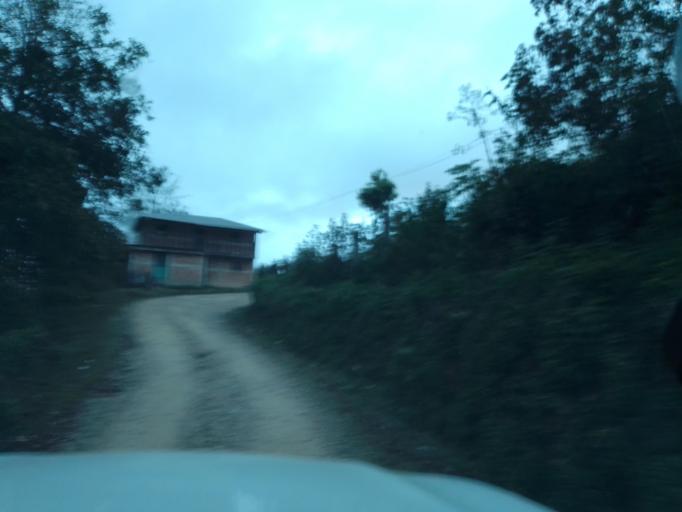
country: MX
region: Chiapas
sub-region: Tapachula
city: Canton Villaflor
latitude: 15.2136
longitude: -92.2361
